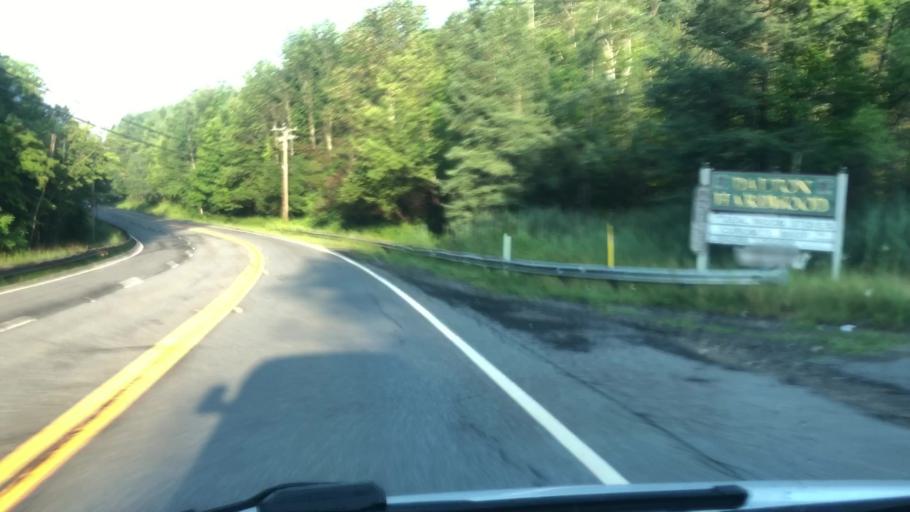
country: US
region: Massachusetts
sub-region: Berkshire County
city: Dalton
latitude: 42.4935
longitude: -73.1164
